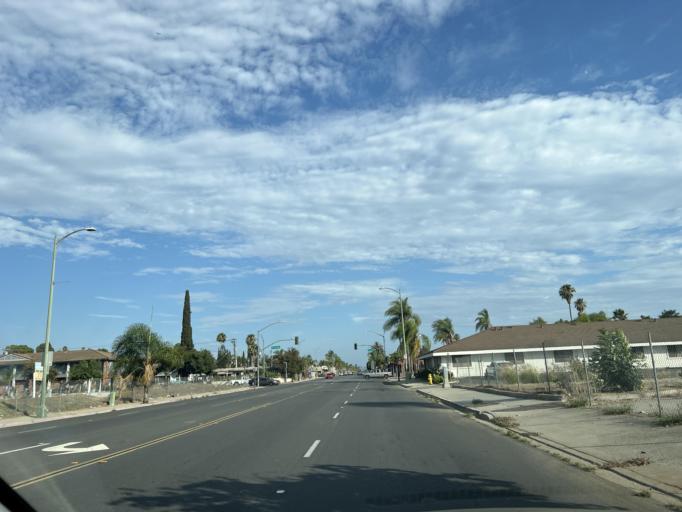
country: US
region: California
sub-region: San Diego County
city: Escondido
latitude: 33.1176
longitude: -117.0821
